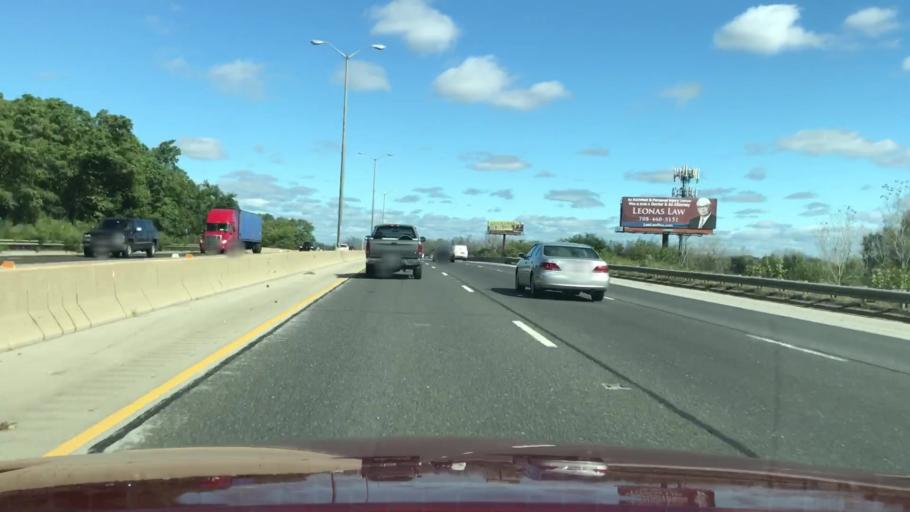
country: US
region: Illinois
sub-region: Cook County
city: South Holland
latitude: 41.6080
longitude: -87.5813
